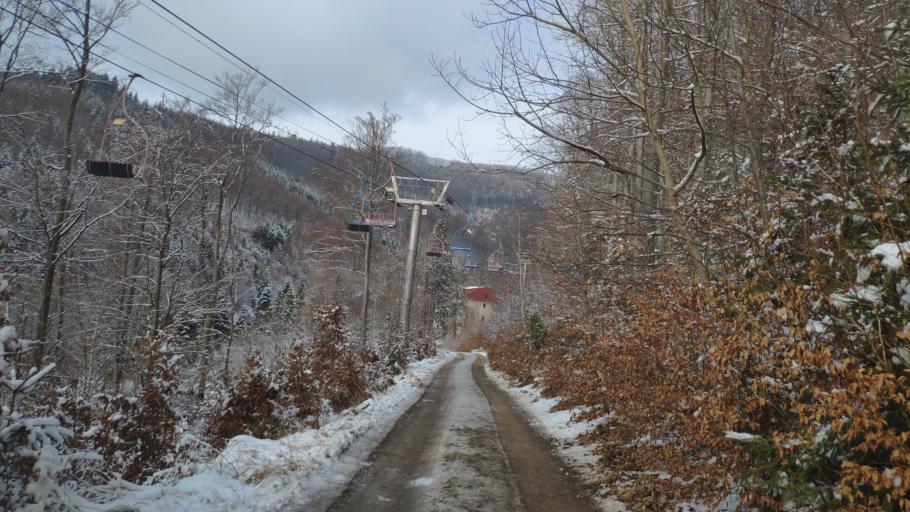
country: SK
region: Kosicky
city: Gelnica
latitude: 48.7621
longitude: 20.9907
